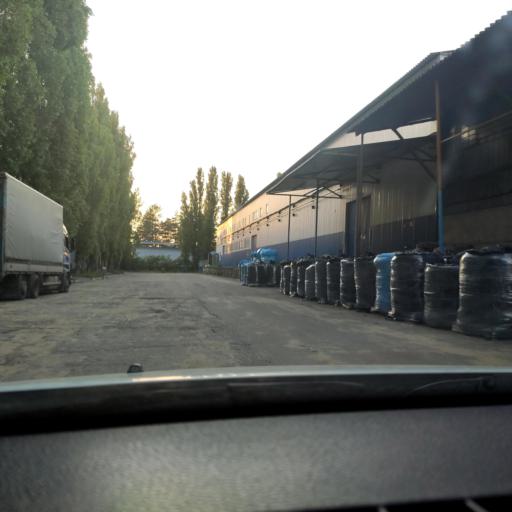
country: RU
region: Voronezj
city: Pridonskoy
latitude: 51.6729
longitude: 39.0853
